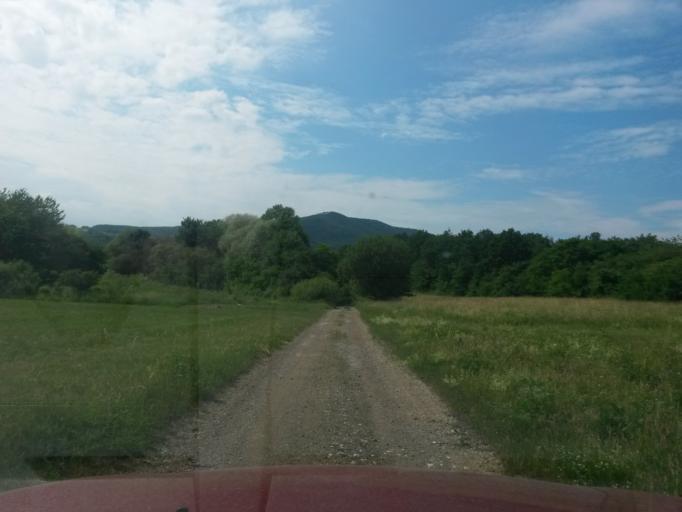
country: SK
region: Kosicky
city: Secovce
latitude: 48.6272
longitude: 21.4989
